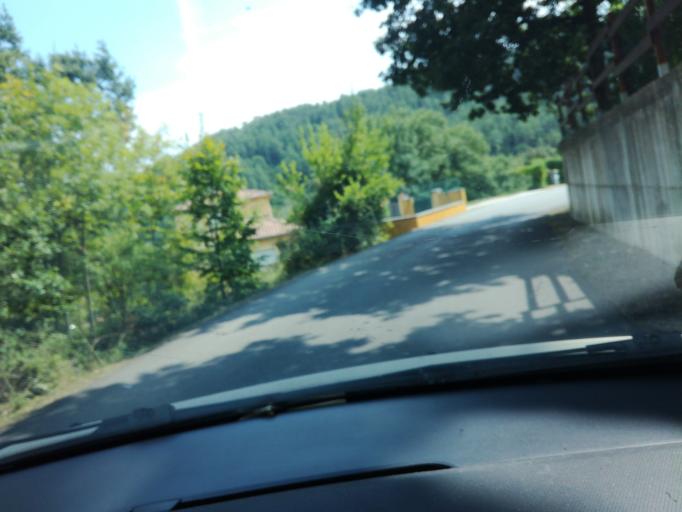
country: FR
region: Rhone-Alpes
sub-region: Departement de l'Ardeche
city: Labegude
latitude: 44.6335
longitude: 4.3635
